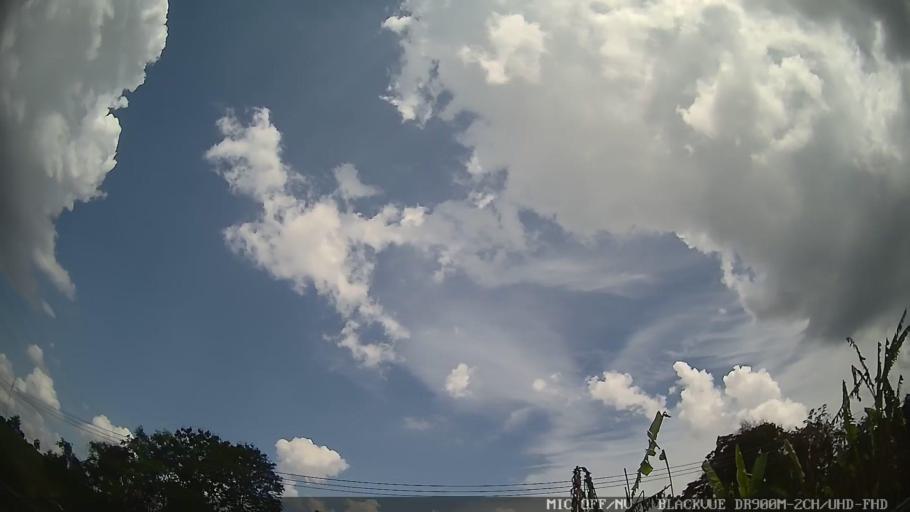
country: BR
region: Sao Paulo
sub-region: Braganca Paulista
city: Braganca Paulista
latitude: -22.9547
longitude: -46.6026
